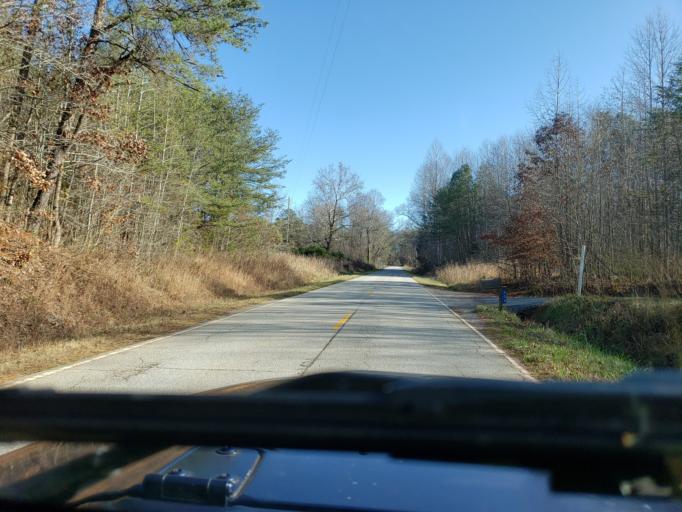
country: US
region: North Carolina
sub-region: Cleveland County
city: White Plains
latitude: 35.1549
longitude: -81.3986
